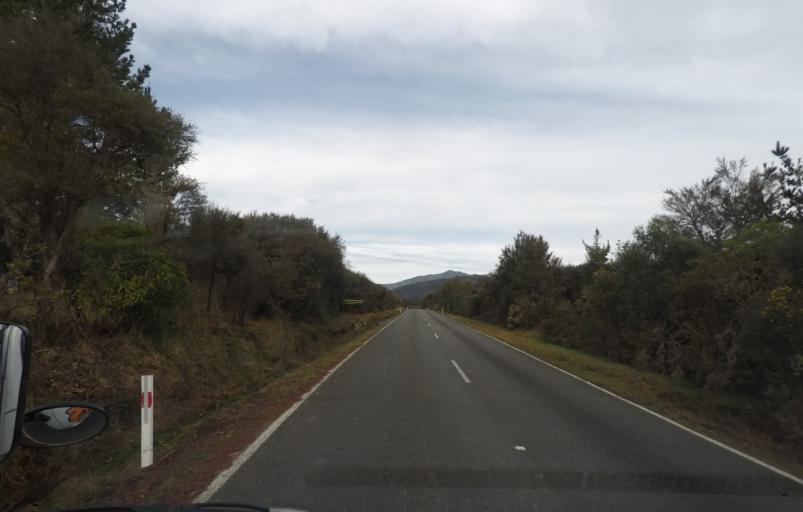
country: NZ
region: Tasman
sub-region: Tasman District
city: Takaka
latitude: -40.8427
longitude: 172.7756
